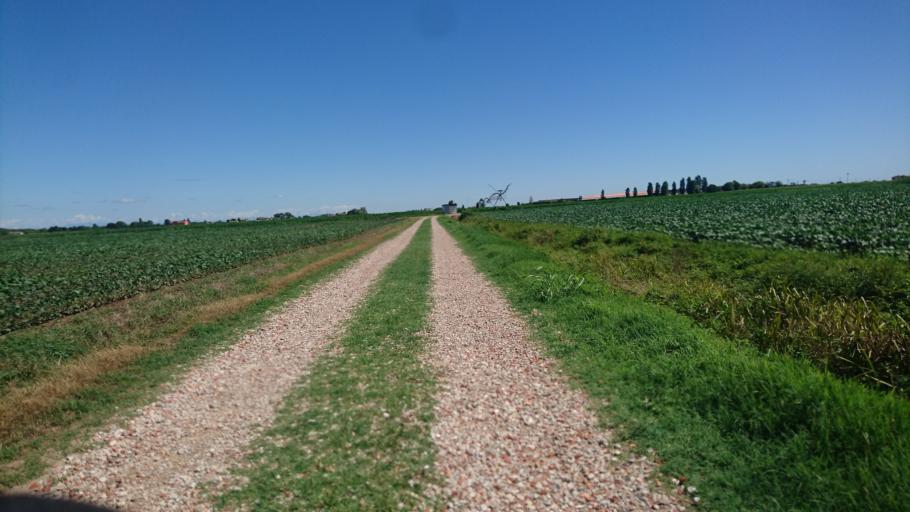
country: IT
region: Veneto
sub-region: Provincia di Padova
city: Pontelongo
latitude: 45.2545
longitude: 12.0102
